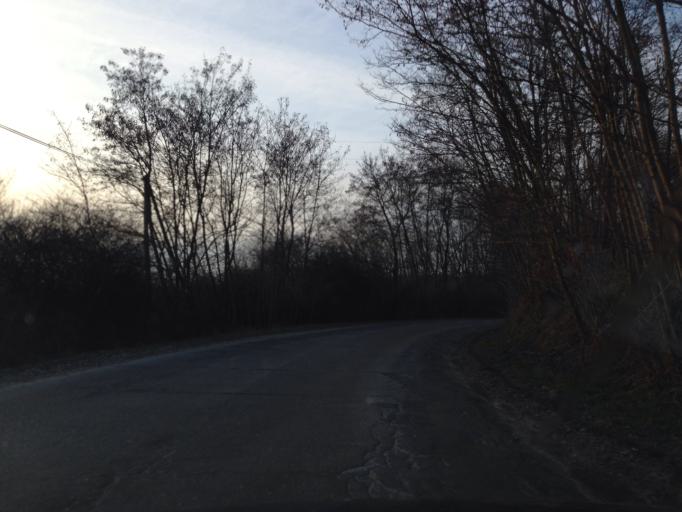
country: PL
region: Greater Poland Voivodeship
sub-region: Powiat poznanski
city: Kostrzyn
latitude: 52.4570
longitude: 17.1664
